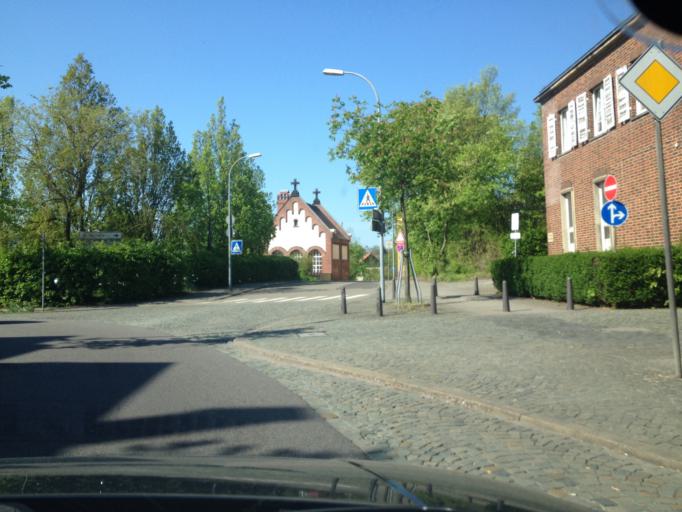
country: DE
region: Saarland
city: Sulzbach
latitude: 49.2992
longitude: 7.0555
